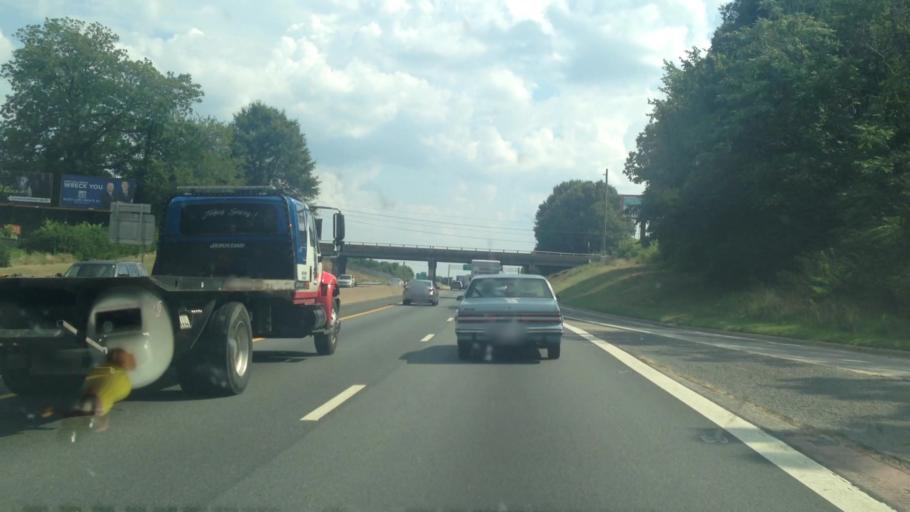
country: US
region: North Carolina
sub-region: Forsyth County
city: Winston-Salem
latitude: 36.1161
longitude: -80.2358
